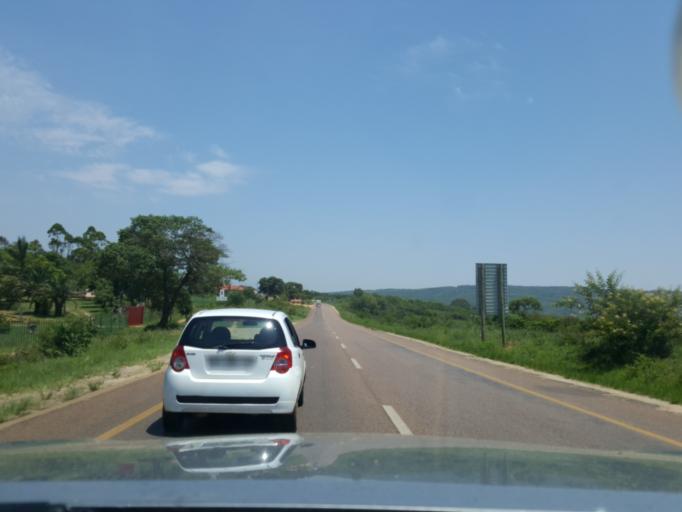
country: ZA
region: Limpopo
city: Thulamahashi
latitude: -24.9085
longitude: 31.1151
